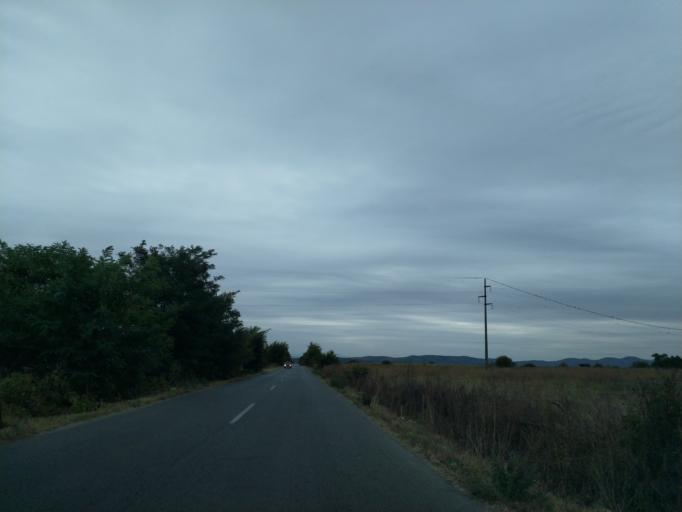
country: RS
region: Central Serbia
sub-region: Pomoravski Okrug
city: Jagodina
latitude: 44.0014
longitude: 21.2125
